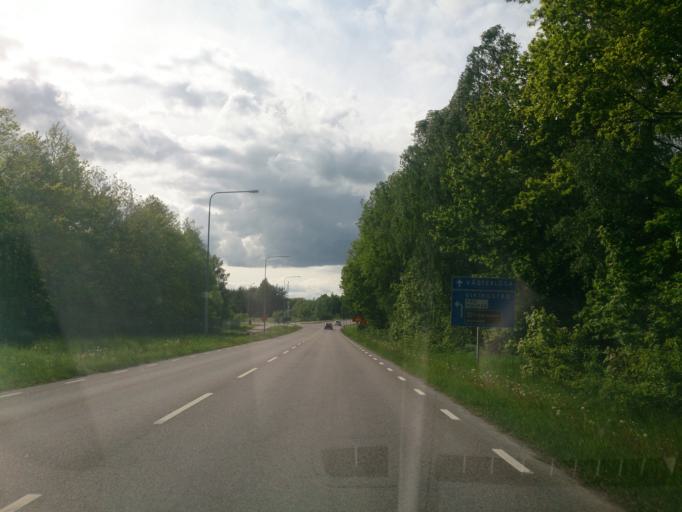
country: SE
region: OEstergoetland
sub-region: Linkopings Kommun
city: Malmslatt
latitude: 58.4107
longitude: 15.5348
